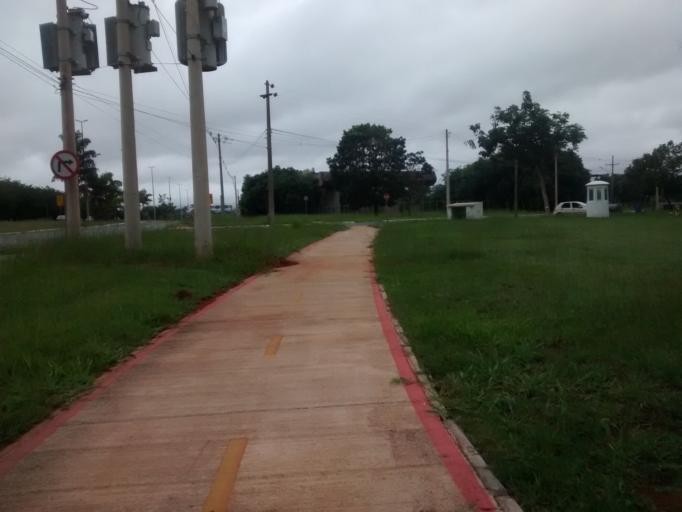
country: BR
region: Federal District
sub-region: Brasilia
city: Brasilia
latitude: -15.7716
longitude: -47.8720
